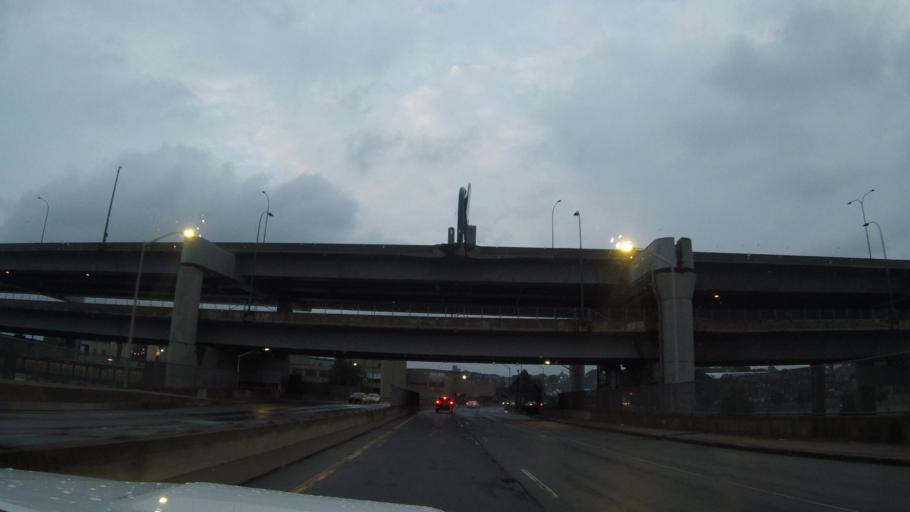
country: US
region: Massachusetts
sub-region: Suffolk County
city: Boston
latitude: 42.3728
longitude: -71.0700
